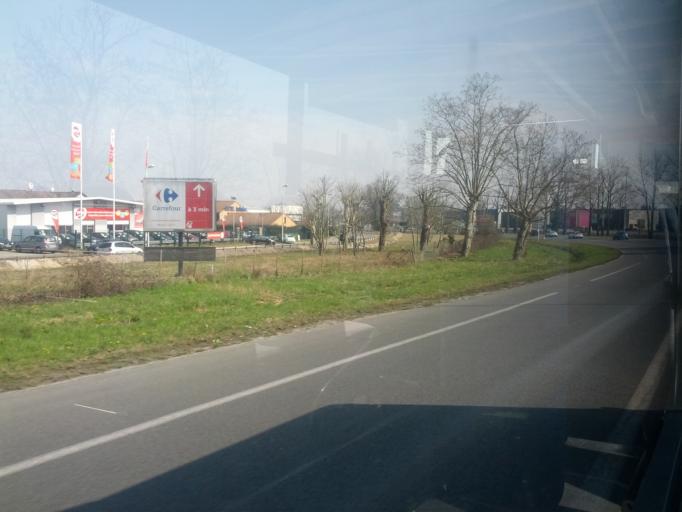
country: FR
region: Aquitaine
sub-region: Departement de la Gironde
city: Pessac
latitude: 44.8319
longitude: -0.6721
